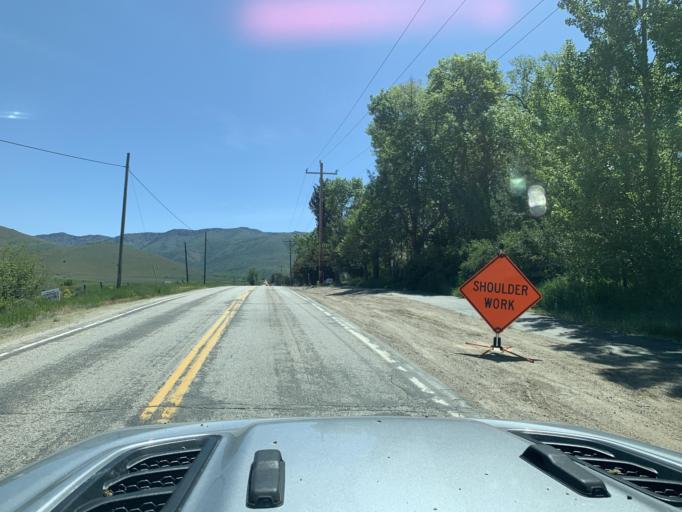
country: US
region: Utah
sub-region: Weber County
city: Wolf Creek
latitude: 41.2932
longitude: -111.7884
